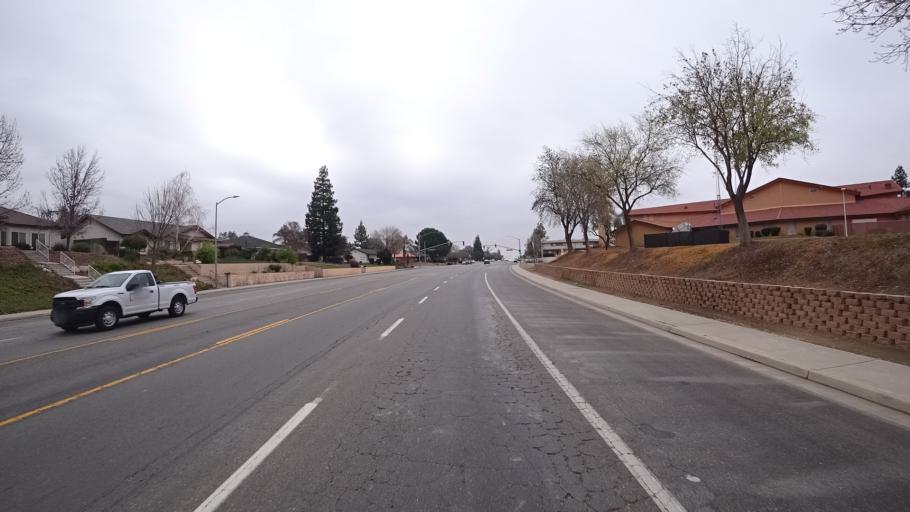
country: US
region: California
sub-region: Kern County
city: Oildale
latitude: 35.4038
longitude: -118.9303
